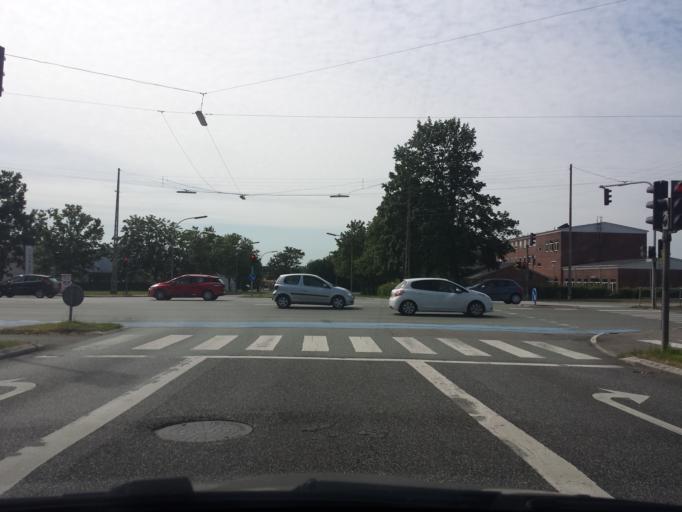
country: DK
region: Capital Region
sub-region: Ballerup Kommune
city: Ballerup
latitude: 55.7278
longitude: 12.3964
